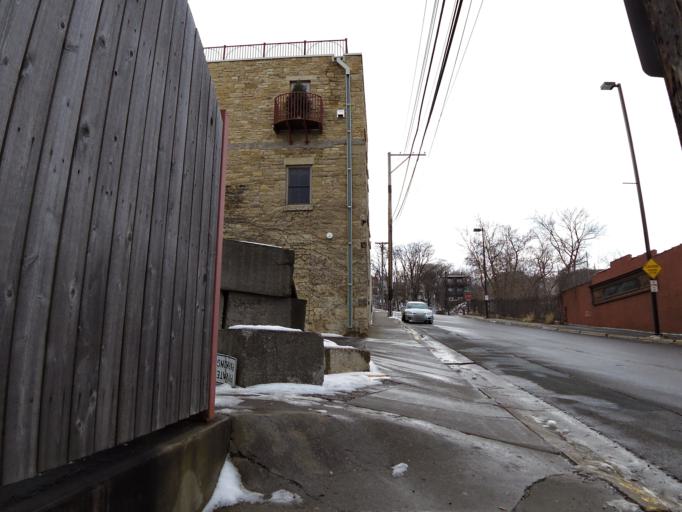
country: US
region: Minnesota
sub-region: Washington County
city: Stillwater
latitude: 45.0541
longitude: -92.8056
